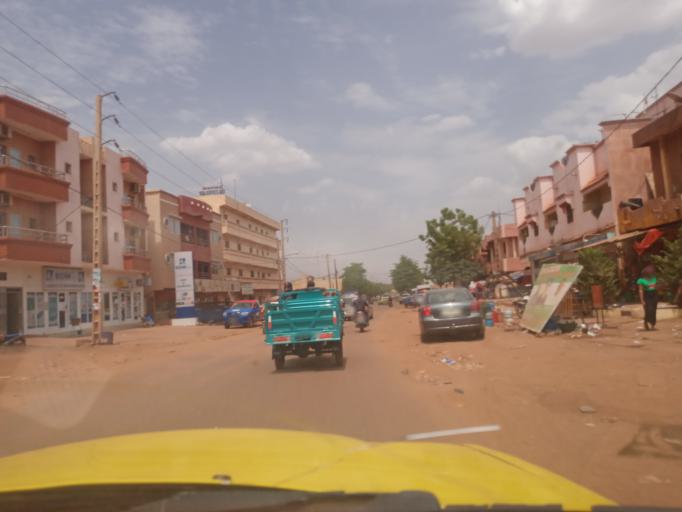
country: ML
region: Bamako
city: Bamako
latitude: 12.6105
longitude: -7.9575
